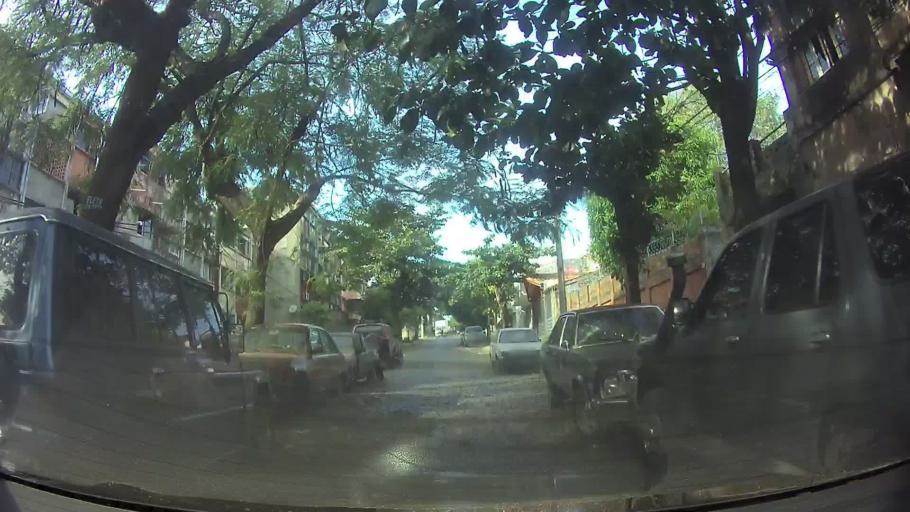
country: PY
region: Presidente Hayes
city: Nanawa
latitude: -25.2824
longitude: -57.6565
